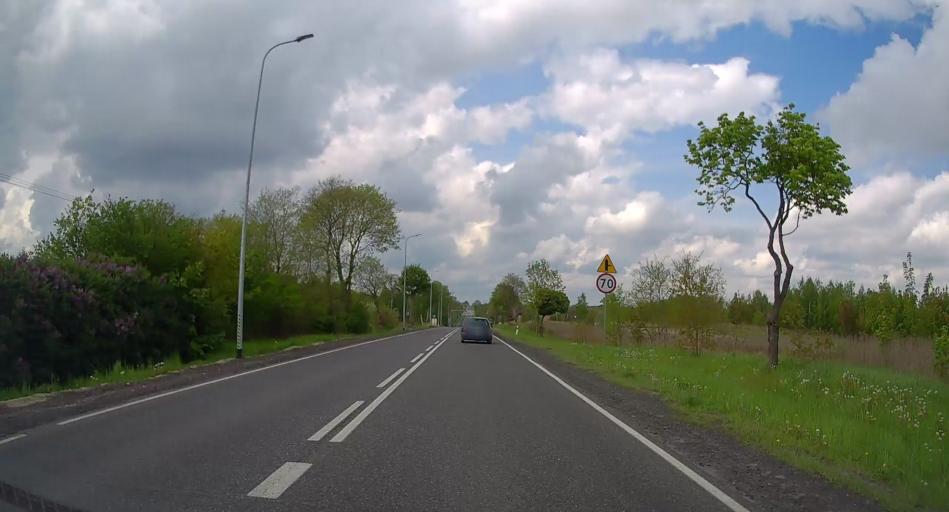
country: PL
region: Masovian Voivodeship
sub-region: Powiat nowodworski
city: Zakroczym
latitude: 52.4414
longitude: 20.5489
